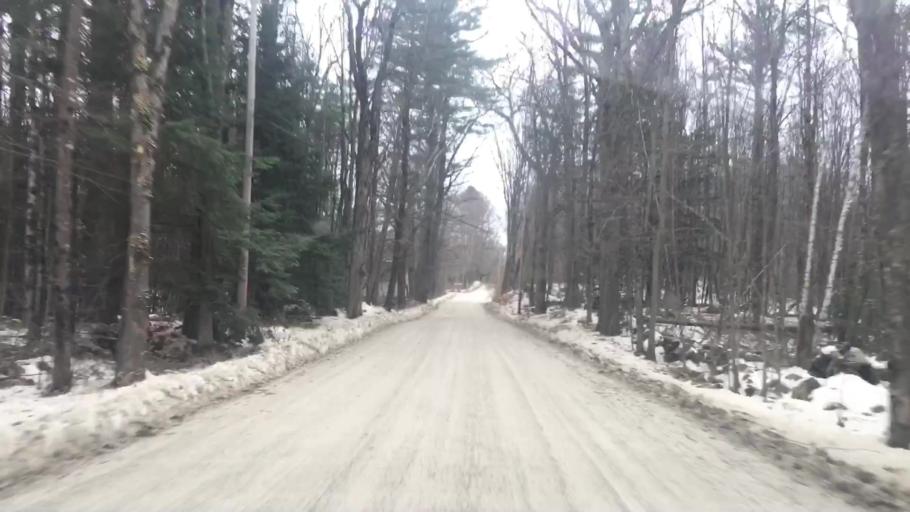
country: US
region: New Hampshire
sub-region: Merrimack County
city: Hopkinton
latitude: 43.1586
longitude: -71.6660
